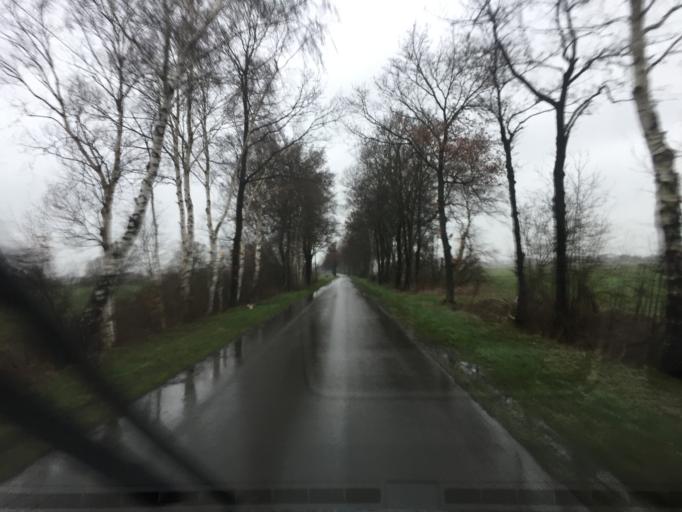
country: DE
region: Lower Saxony
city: Siedenburg
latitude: 52.6505
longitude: 8.9231
